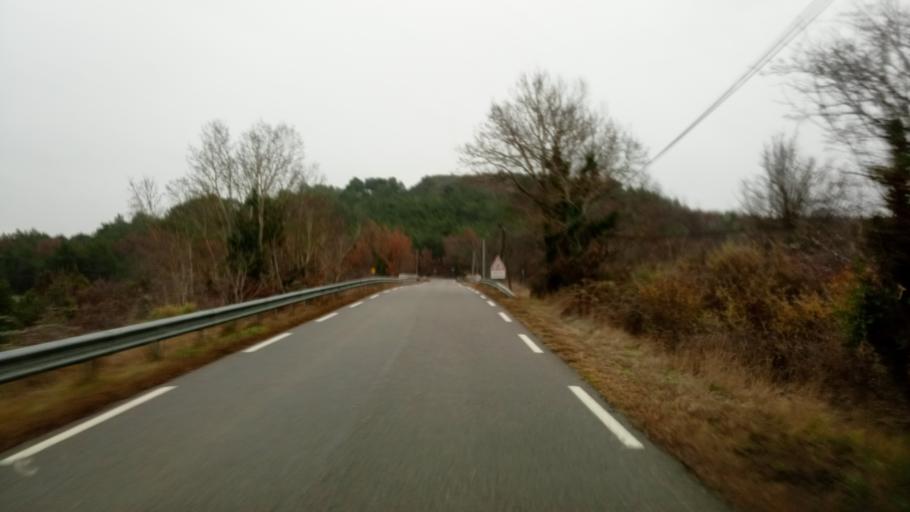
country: FR
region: Provence-Alpes-Cote d'Azur
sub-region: Departement du Var
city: Ginasservis
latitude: 43.7094
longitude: 5.8666
